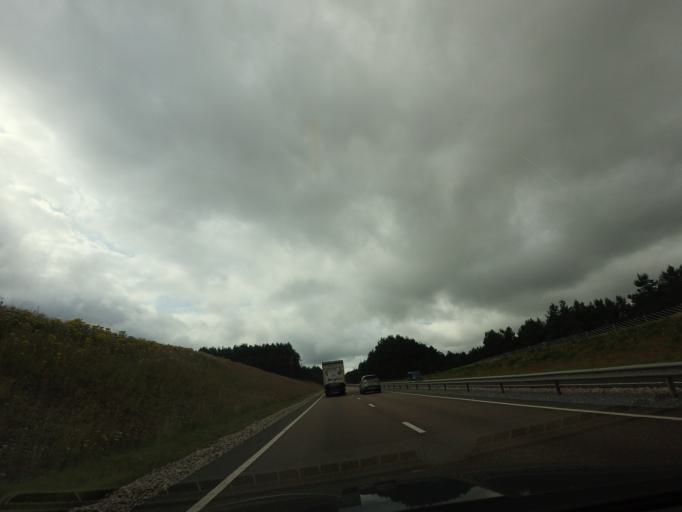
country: GB
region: Scotland
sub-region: Highland
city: Aviemore
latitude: 57.1545
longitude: -3.9005
